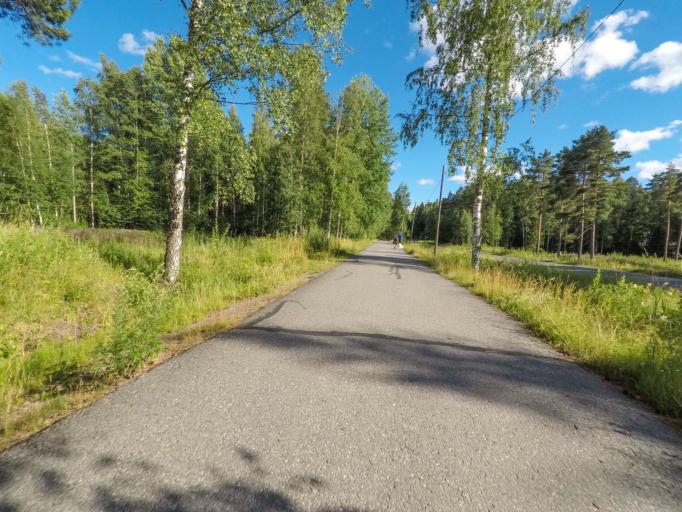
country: FI
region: South Karelia
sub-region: Lappeenranta
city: Lappeenranta
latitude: 61.0875
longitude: 28.1444
